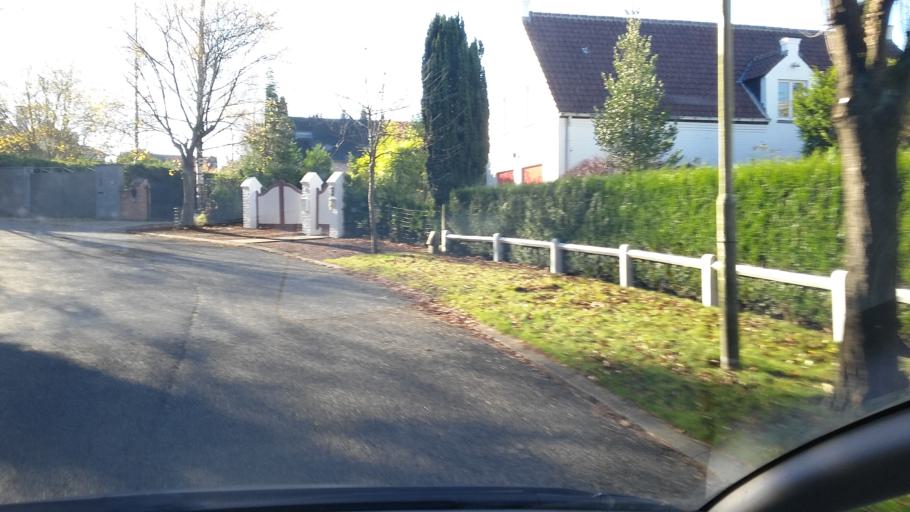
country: BE
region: Wallonia
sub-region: Province du Brabant Wallon
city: Waterloo
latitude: 50.7074
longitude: 4.4153
